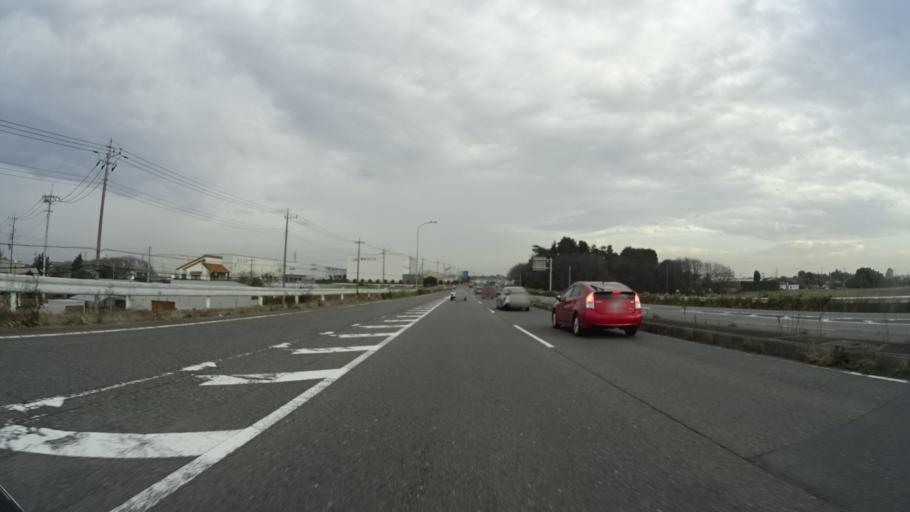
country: JP
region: Gunma
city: Isesaki
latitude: 36.3648
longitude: 139.1771
